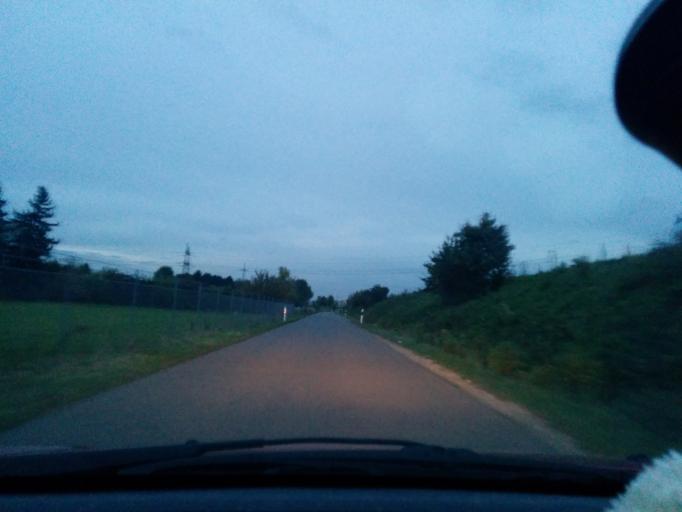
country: DE
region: Bavaria
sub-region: Upper Bavaria
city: Karlsfeld
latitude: 48.2047
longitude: 11.4335
